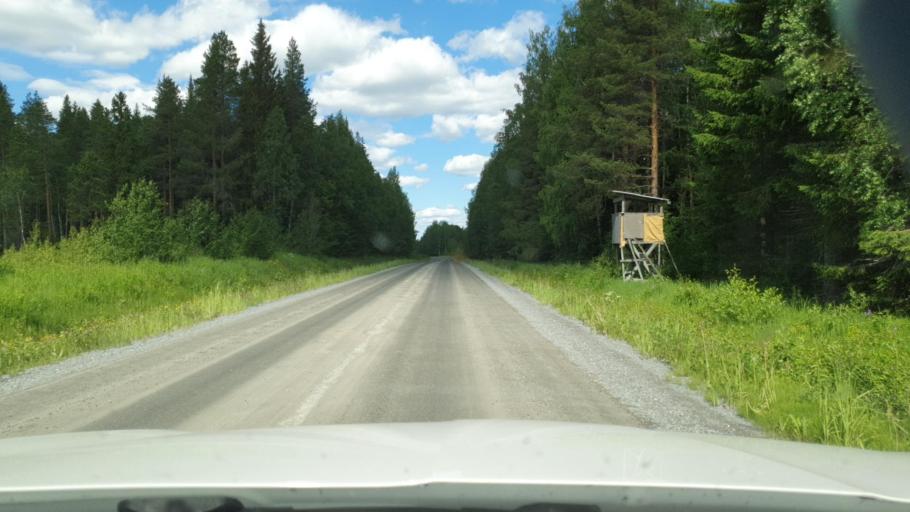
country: SE
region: Vaesterbotten
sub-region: Skelleftea Kommun
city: Forsbacka
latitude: 64.8287
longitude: 20.4992
